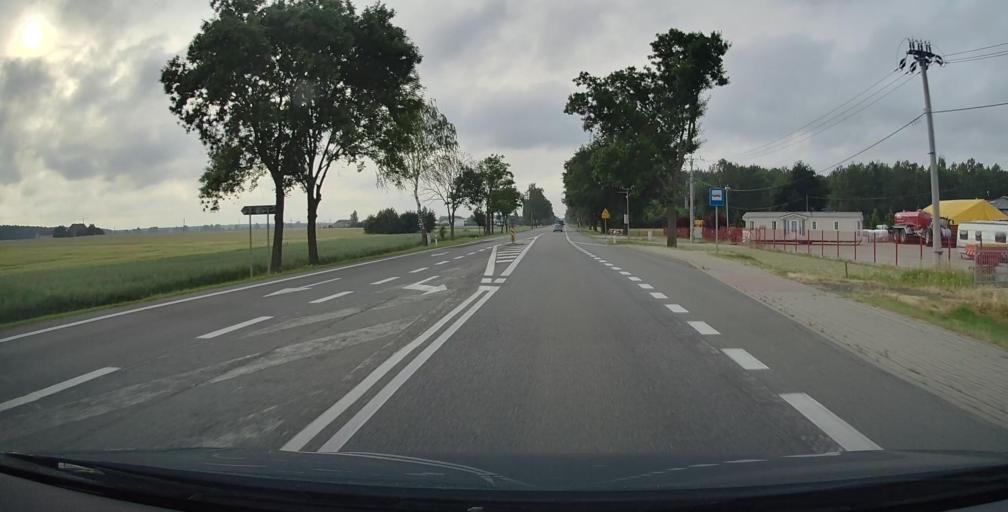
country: PL
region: Masovian Voivodeship
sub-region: Powiat siedlecki
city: Zbuczyn
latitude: 52.0997
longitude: 22.4067
